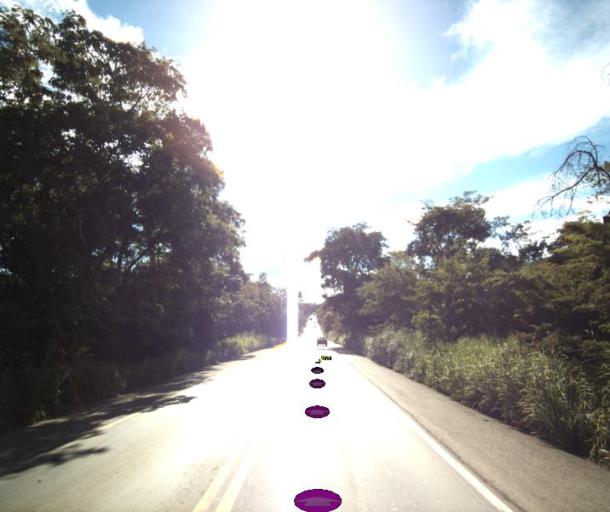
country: BR
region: Goias
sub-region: Uruana
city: Uruana
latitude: -15.5279
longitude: -49.4578
